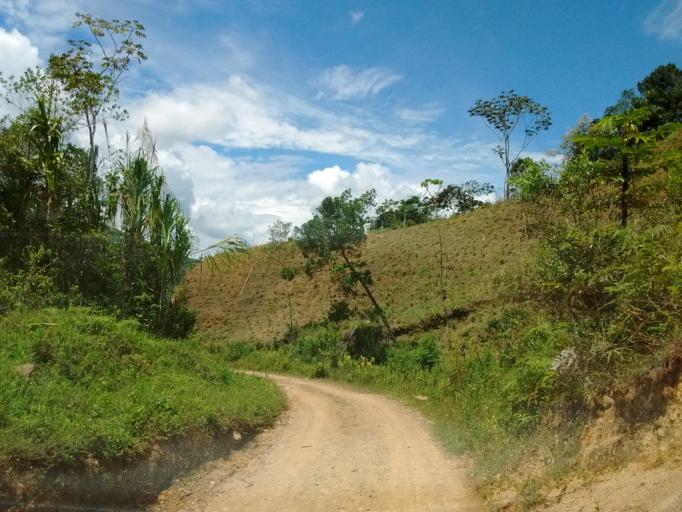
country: CO
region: Cauca
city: Villa Rica
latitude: 2.6645
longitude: -76.7660
